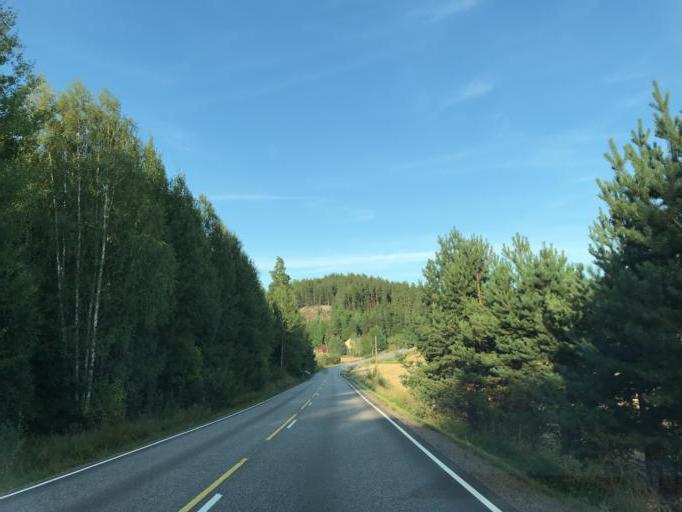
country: FI
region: Uusimaa
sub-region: Helsinki
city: Vihti
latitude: 60.4169
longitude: 24.3955
